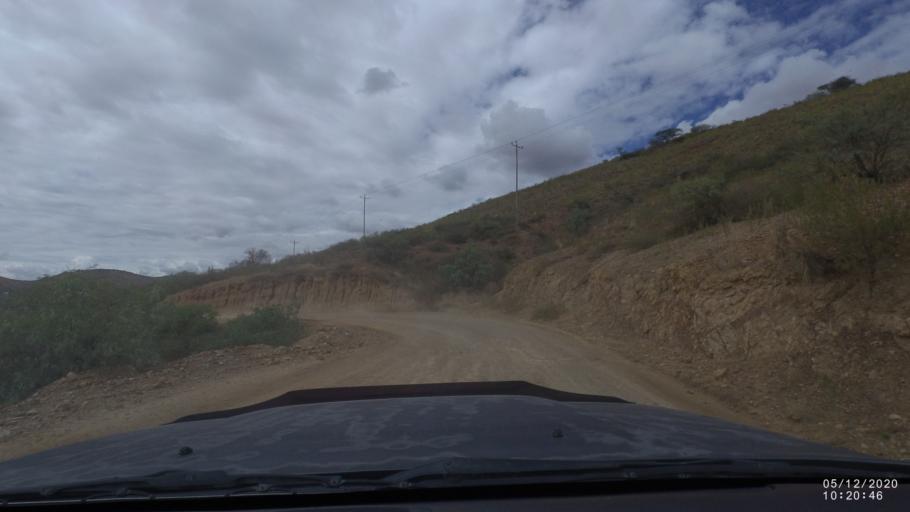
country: BO
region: Cochabamba
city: Sipe Sipe
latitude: -17.4856
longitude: -66.2825
